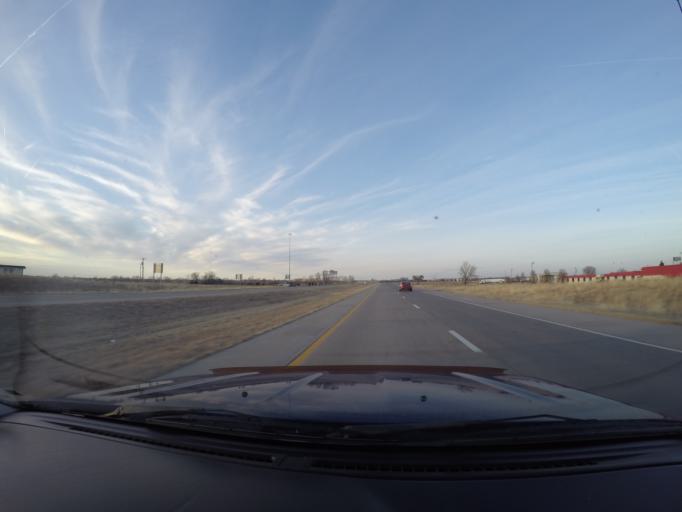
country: US
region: Kansas
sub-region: Saline County
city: Salina
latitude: 38.8284
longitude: -97.6401
